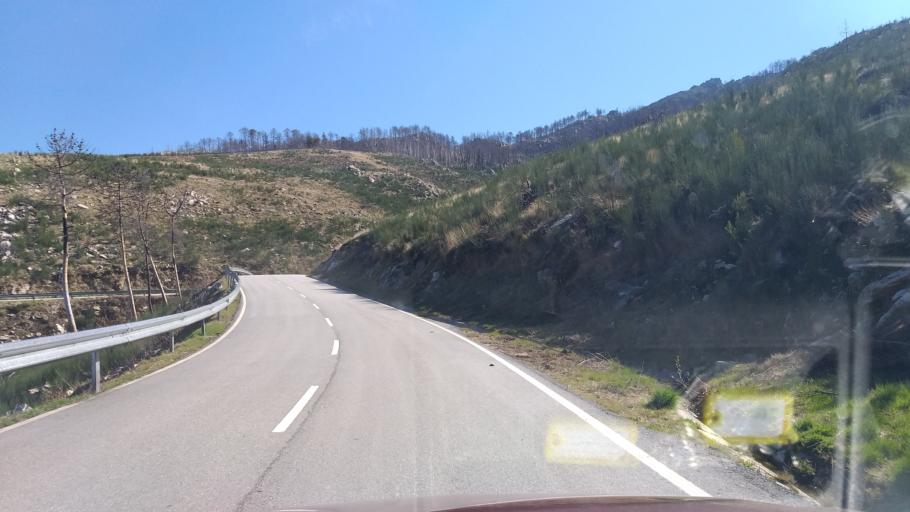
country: PT
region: Guarda
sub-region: Manteigas
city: Manteigas
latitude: 40.4950
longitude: -7.5272
